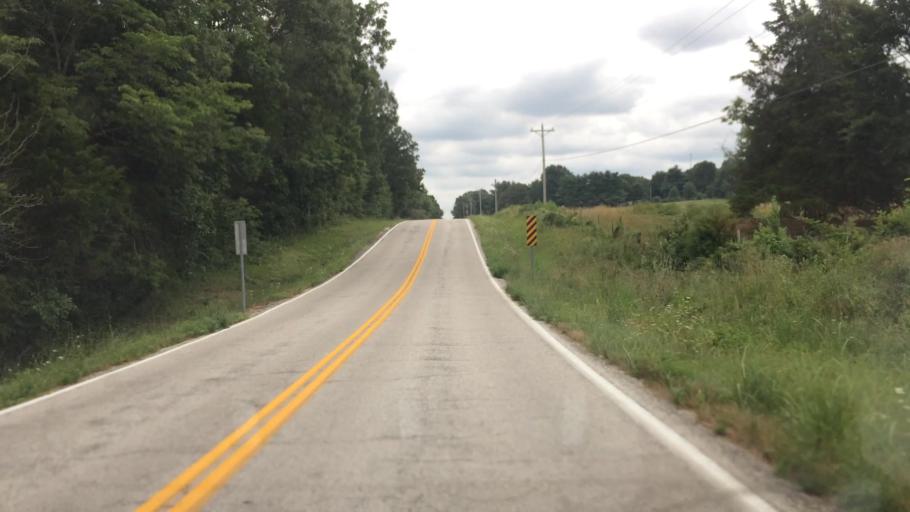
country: US
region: Missouri
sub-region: Greene County
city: Strafford
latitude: 37.2942
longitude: -93.2074
